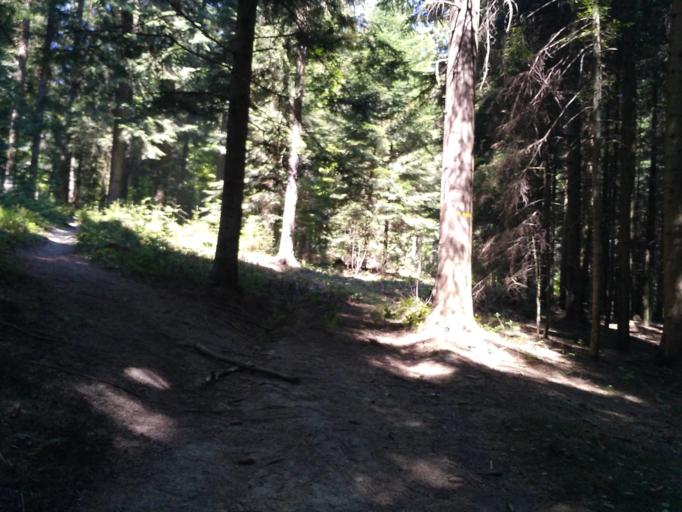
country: PL
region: Subcarpathian Voivodeship
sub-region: Powiat krosnienski
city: Korczyna
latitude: 49.7354
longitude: 21.8593
